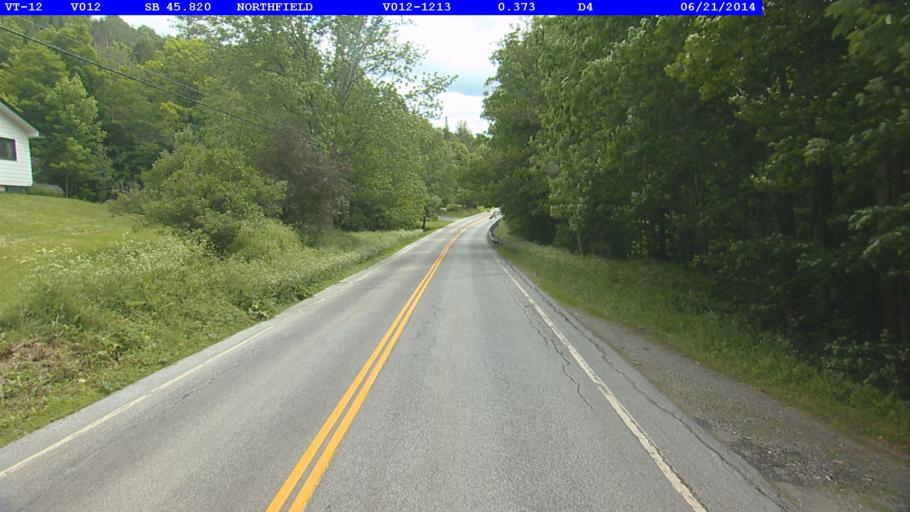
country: US
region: Vermont
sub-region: Washington County
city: Northfield
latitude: 44.0979
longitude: -72.6446
